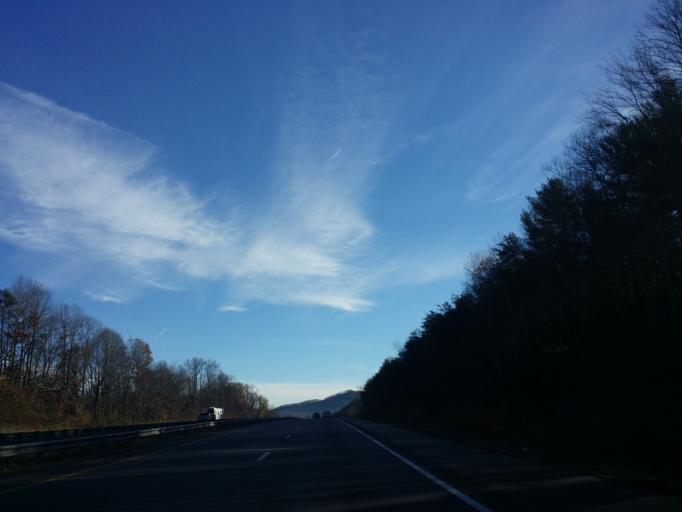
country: US
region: North Carolina
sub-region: Buncombe County
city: Swannanoa
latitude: 35.6001
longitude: -82.3633
